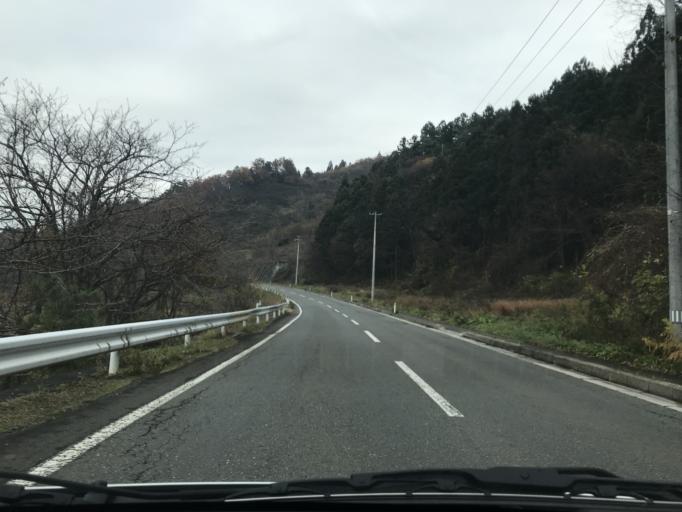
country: JP
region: Iwate
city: Mizusawa
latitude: 39.1806
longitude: 141.2195
